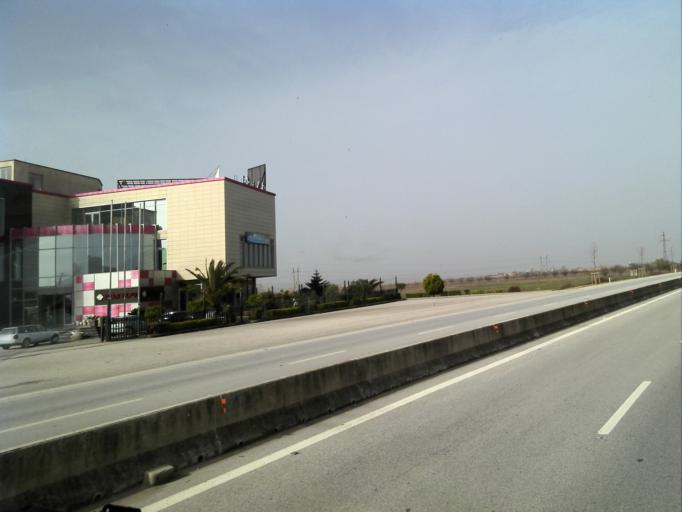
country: AL
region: Fier
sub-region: Rrethi i Lushnjes
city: Lushnje
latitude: 40.9332
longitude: 19.6859
